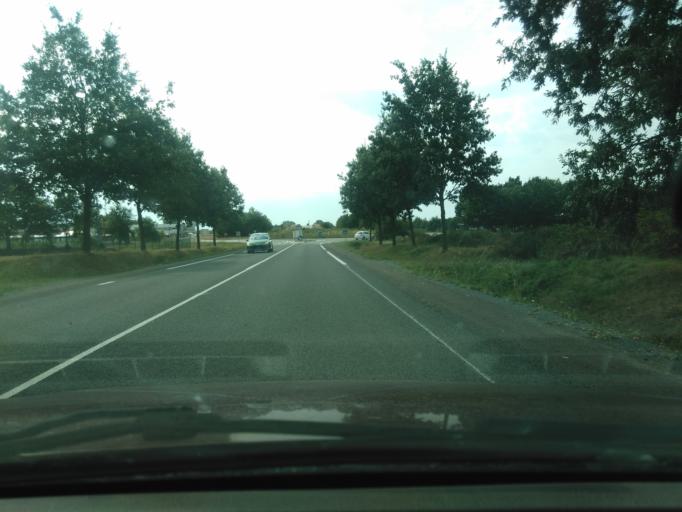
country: FR
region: Pays de la Loire
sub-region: Departement de la Vendee
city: Belleville-sur-Vie
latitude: 46.7449
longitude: -1.4251
